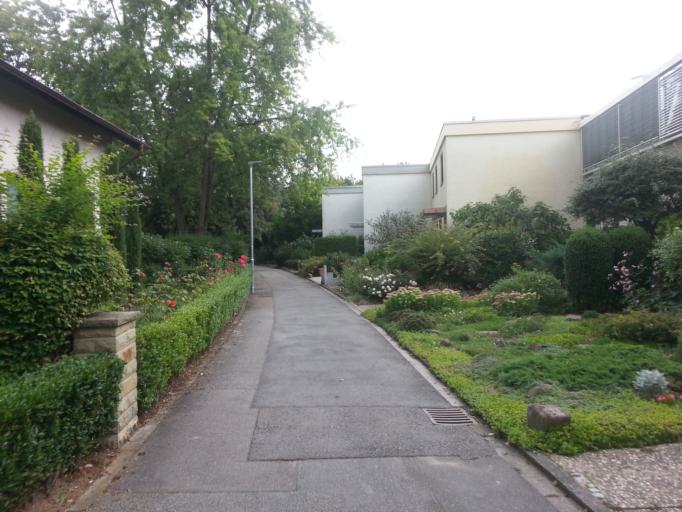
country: DE
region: Baden-Wuerttemberg
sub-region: Karlsruhe Region
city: Ladenburg
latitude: 49.4697
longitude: 8.6150
